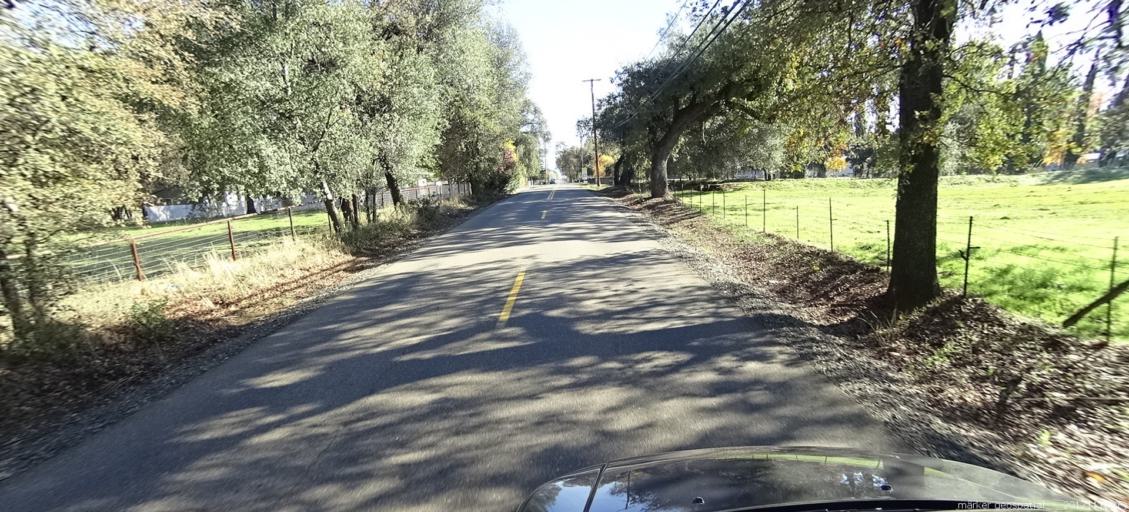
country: US
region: California
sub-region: Shasta County
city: Cottonwood
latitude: 40.3857
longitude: -122.2950
